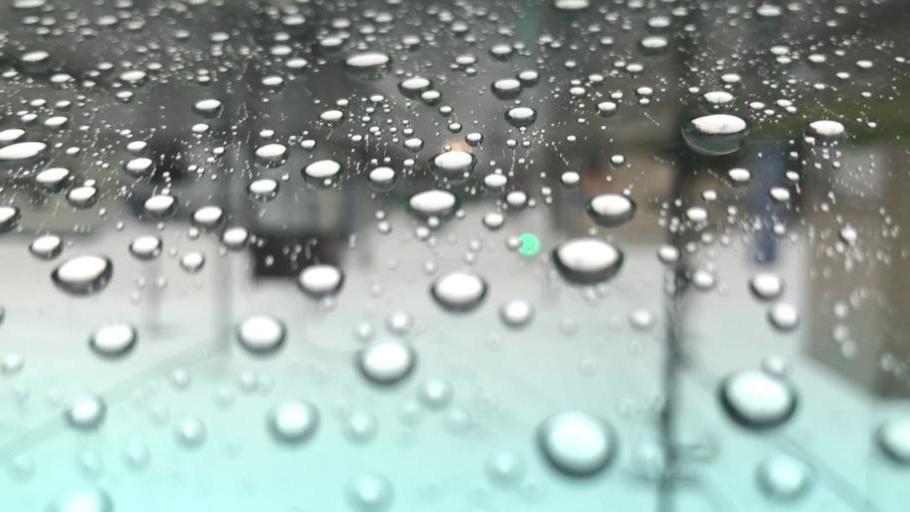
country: JP
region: Hokkaido
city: Nayoro
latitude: 44.2921
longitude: 142.4193
